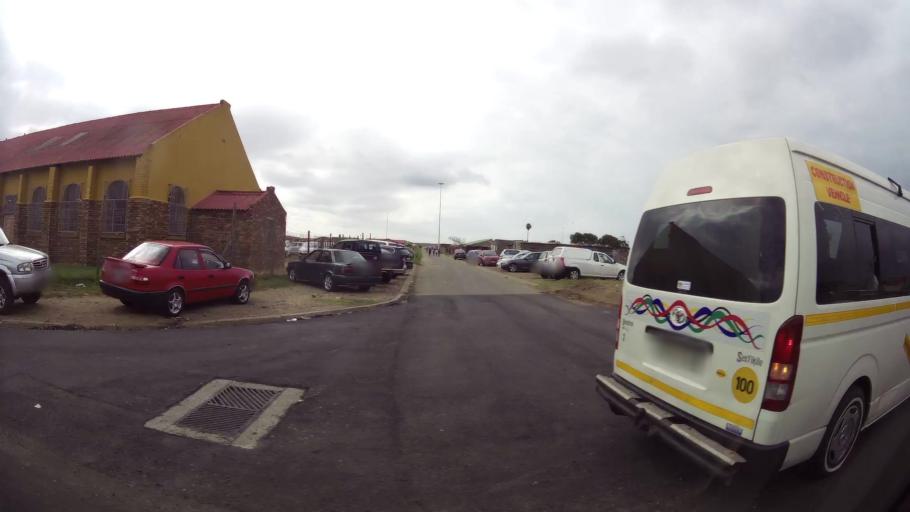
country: ZA
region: Eastern Cape
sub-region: Nelson Mandela Bay Metropolitan Municipality
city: Port Elizabeth
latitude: -33.8648
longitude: 25.5777
